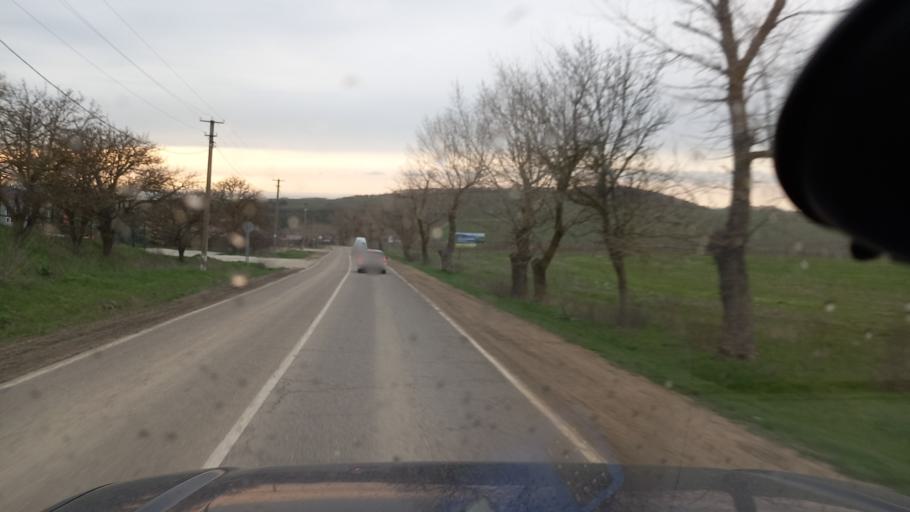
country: RU
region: Krasnodarskiy
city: Sukko
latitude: 44.8411
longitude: 37.3929
